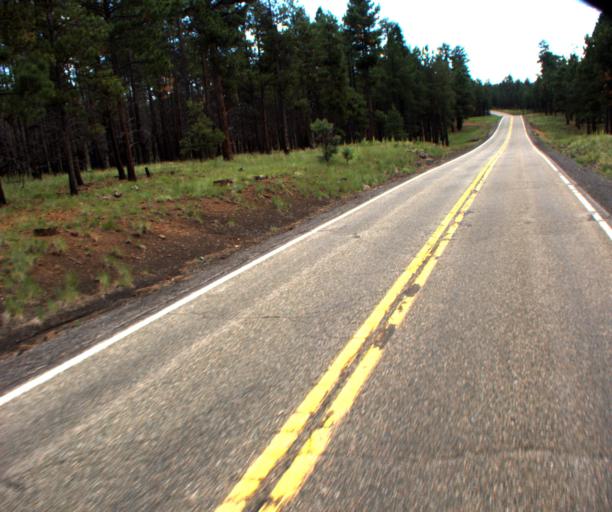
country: US
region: Arizona
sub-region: Coconino County
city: Parks
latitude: 35.3363
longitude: -111.7844
